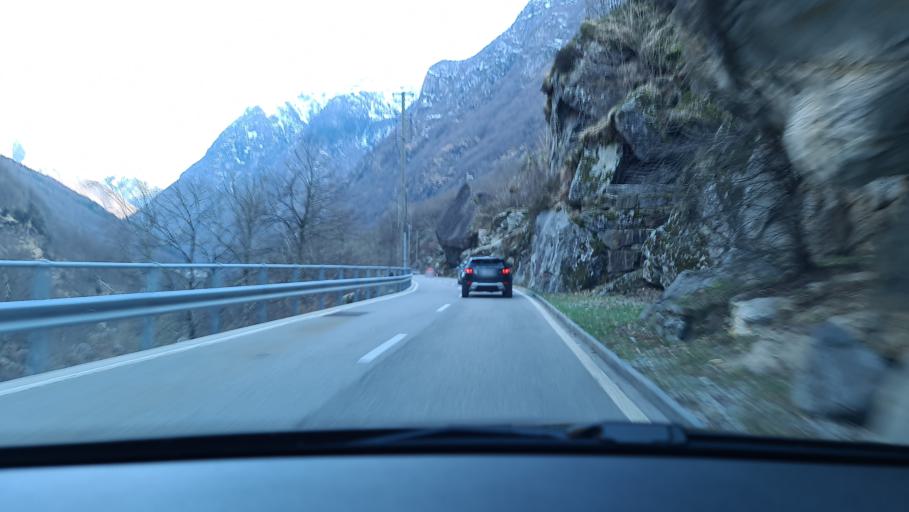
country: CH
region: Ticino
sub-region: Locarno District
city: Lavertezzo
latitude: 46.2898
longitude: 8.7955
